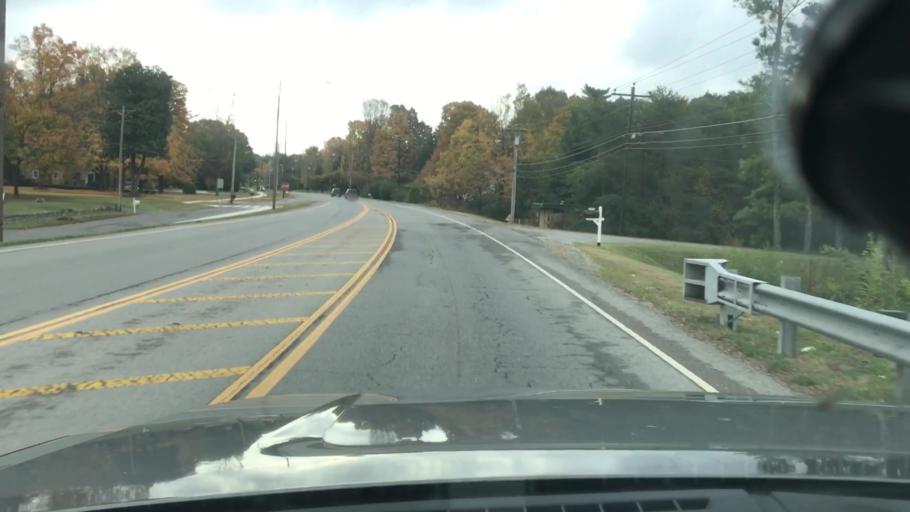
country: US
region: Tennessee
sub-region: Williamson County
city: Franklin
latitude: 35.9194
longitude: -86.8631
